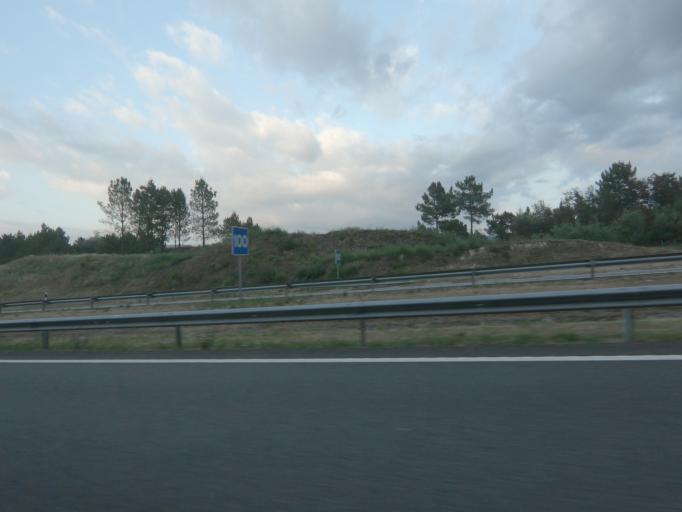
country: ES
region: Galicia
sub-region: Provincia de Ourense
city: Punxin
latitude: 42.3411
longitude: -8.0139
